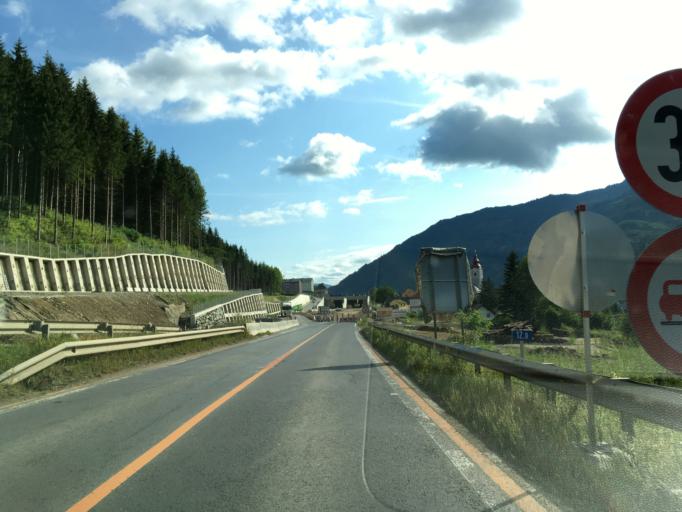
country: AT
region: Styria
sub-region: Politischer Bezirk Murtal
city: Sankt Georgen ob Judenburg
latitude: 47.2023
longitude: 14.4503
